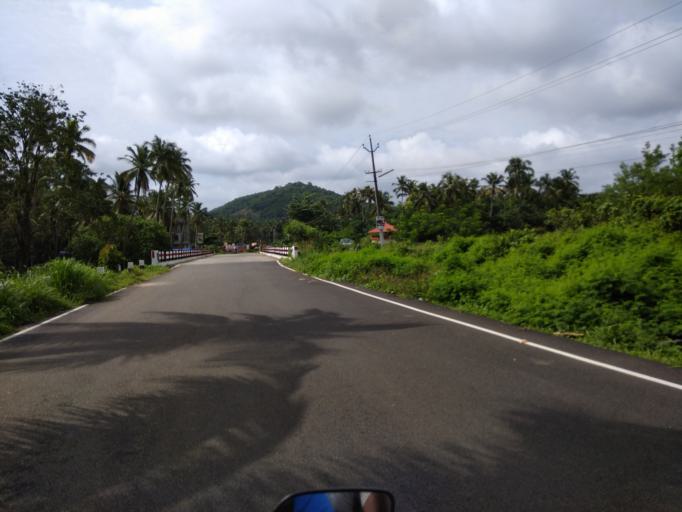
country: IN
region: Kerala
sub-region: Thrissur District
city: Trichur
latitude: 10.5376
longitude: 76.3339
